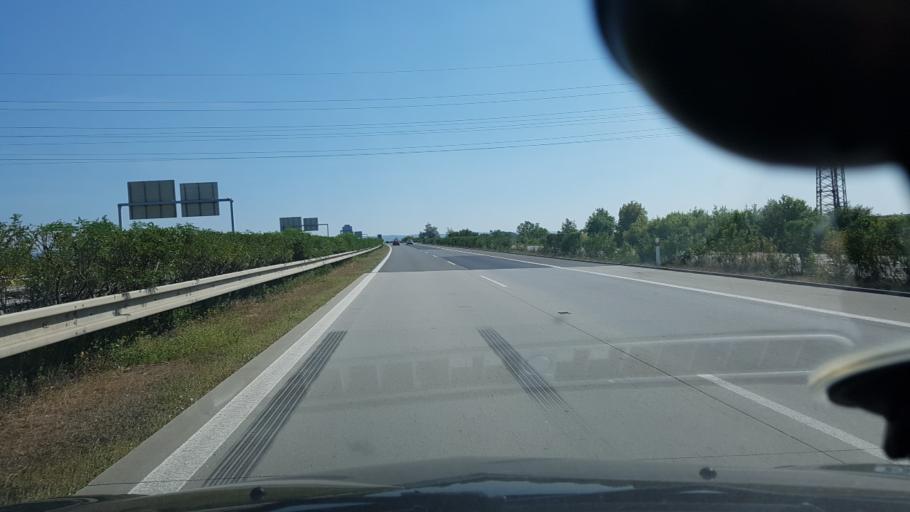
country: CZ
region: Olomoucky
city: Velky Tynec
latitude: 49.5605
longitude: 17.3194
